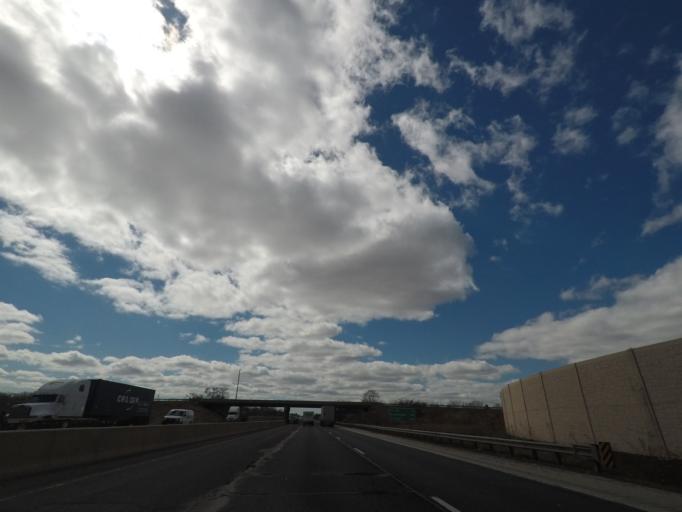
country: US
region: Illinois
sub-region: Will County
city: Crystal Lawns
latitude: 41.5665
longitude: -88.1811
